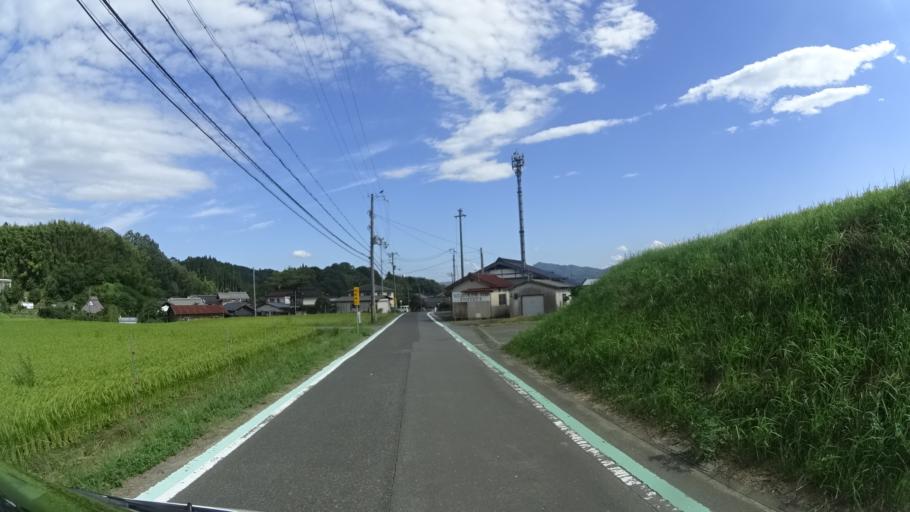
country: JP
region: Kyoto
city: Fukuchiyama
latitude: 35.3293
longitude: 135.1751
